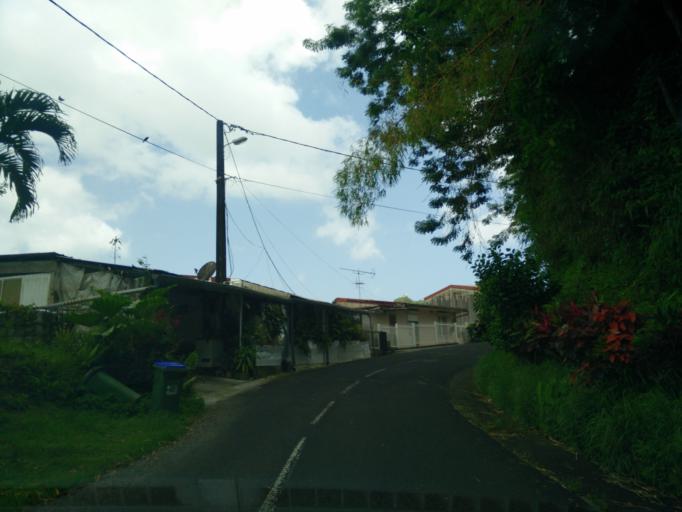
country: MQ
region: Martinique
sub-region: Martinique
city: Le Morne-Rouge
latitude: 14.7333
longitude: -61.1317
